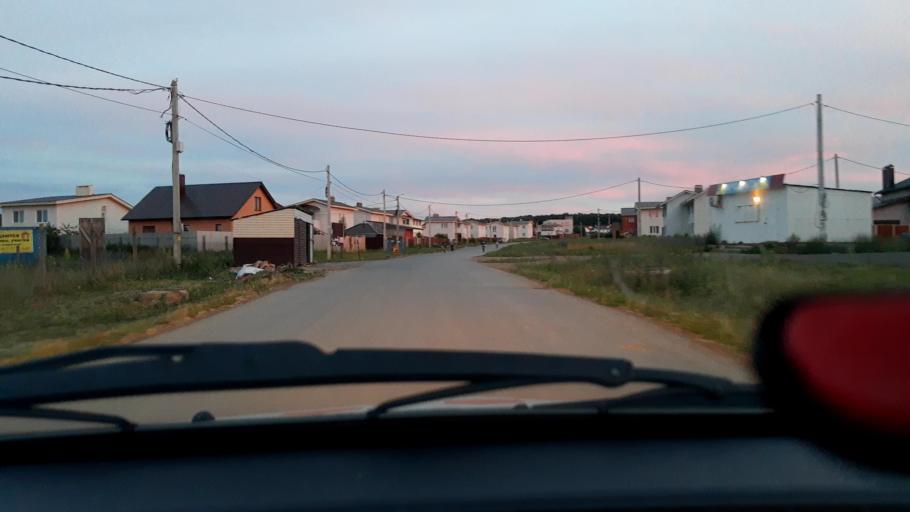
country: RU
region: Bashkortostan
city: Avdon
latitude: 54.4828
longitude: 55.8795
